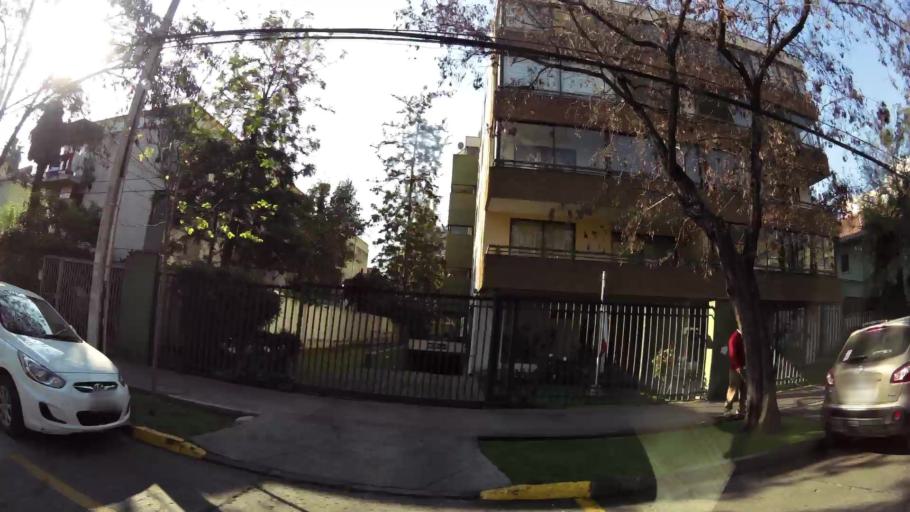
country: CL
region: Santiago Metropolitan
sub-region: Provincia de Santiago
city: Villa Presidente Frei, Nunoa, Santiago, Chile
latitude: -33.4401
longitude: -70.6052
